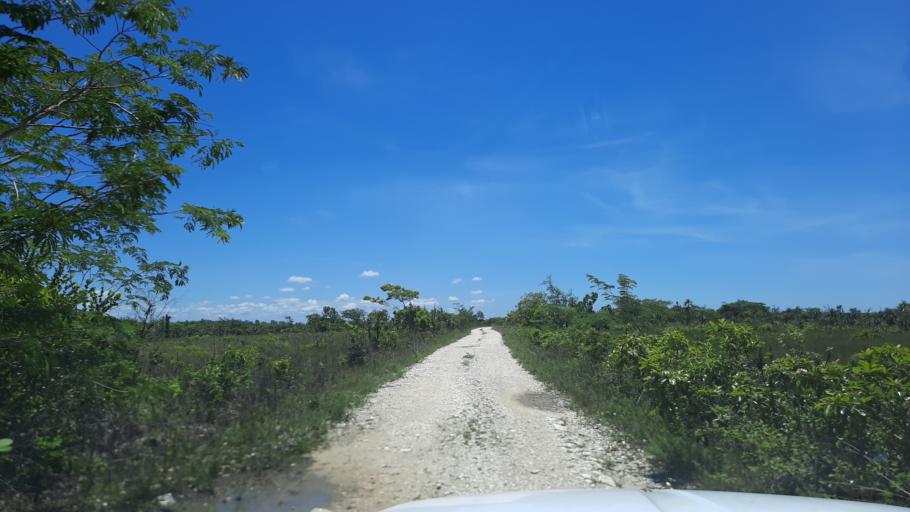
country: BZ
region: Cayo
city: Belmopan
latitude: 17.3833
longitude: -88.4959
